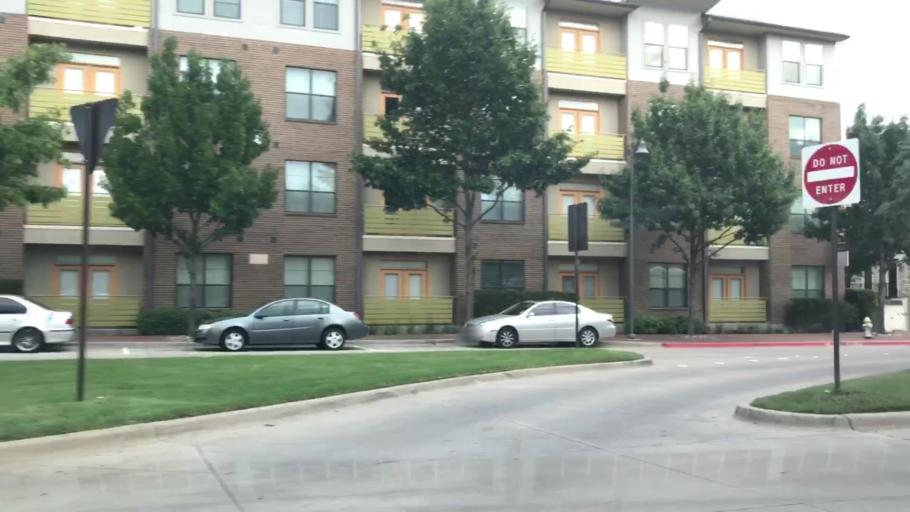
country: US
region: Texas
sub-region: Denton County
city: The Colony
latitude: 33.0800
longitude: -96.8213
